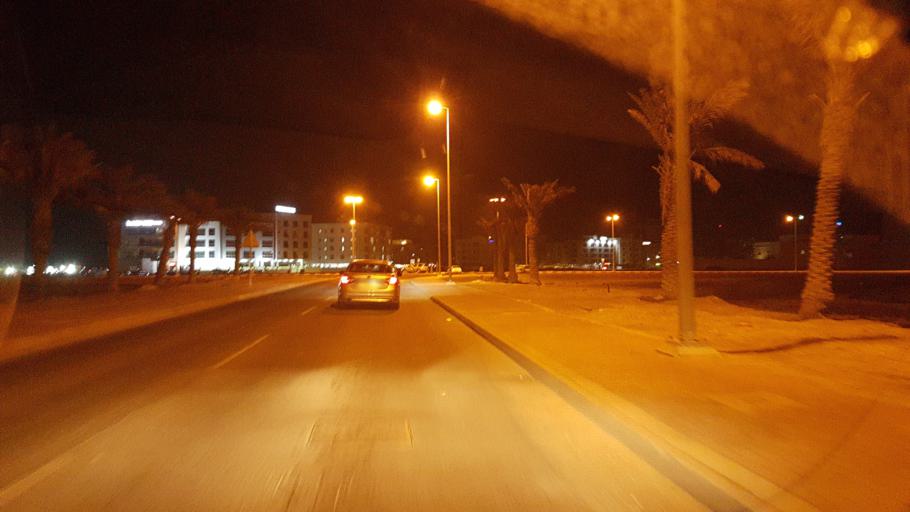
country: BH
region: Manama
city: Jidd Hafs
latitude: 26.2363
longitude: 50.5250
